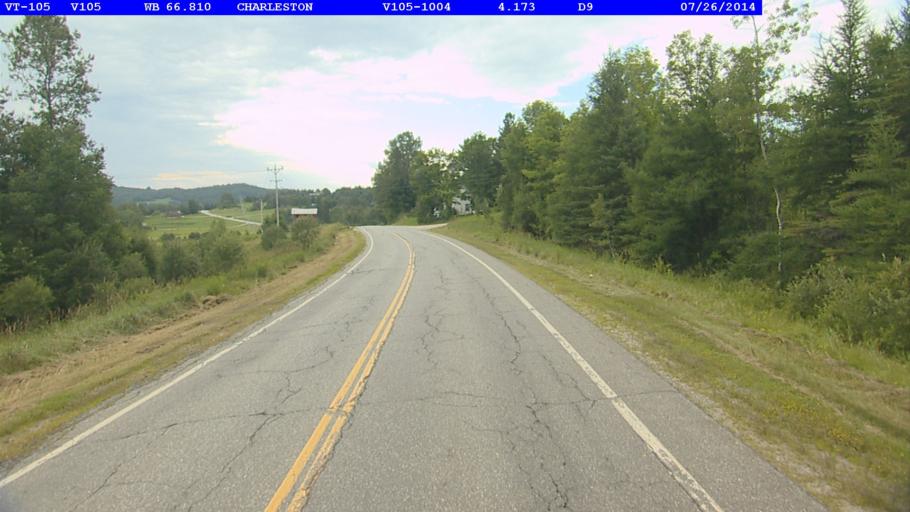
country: US
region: Vermont
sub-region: Orleans County
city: Newport
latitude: 44.8605
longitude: -72.0357
